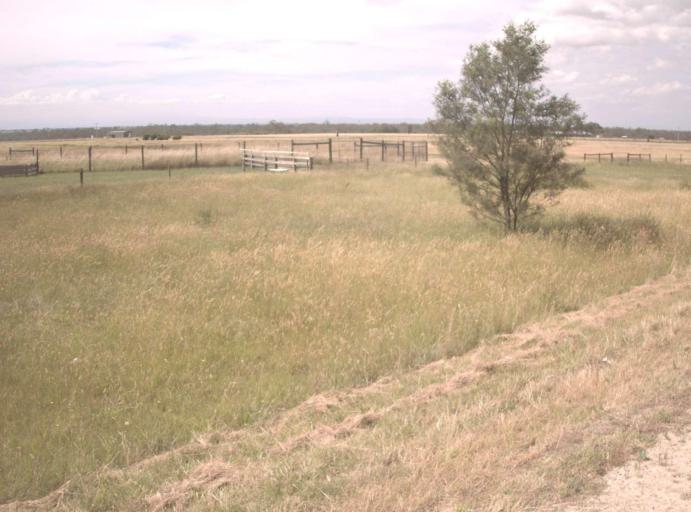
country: AU
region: Victoria
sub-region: Wellington
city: Sale
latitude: -38.1688
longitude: 147.0359
